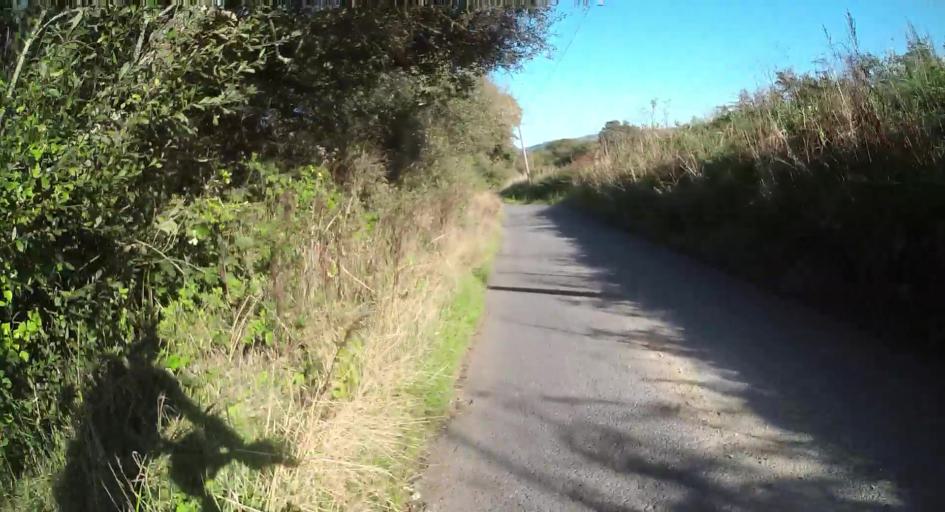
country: GB
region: England
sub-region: Isle of Wight
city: Chale
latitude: 50.6416
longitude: -1.3107
